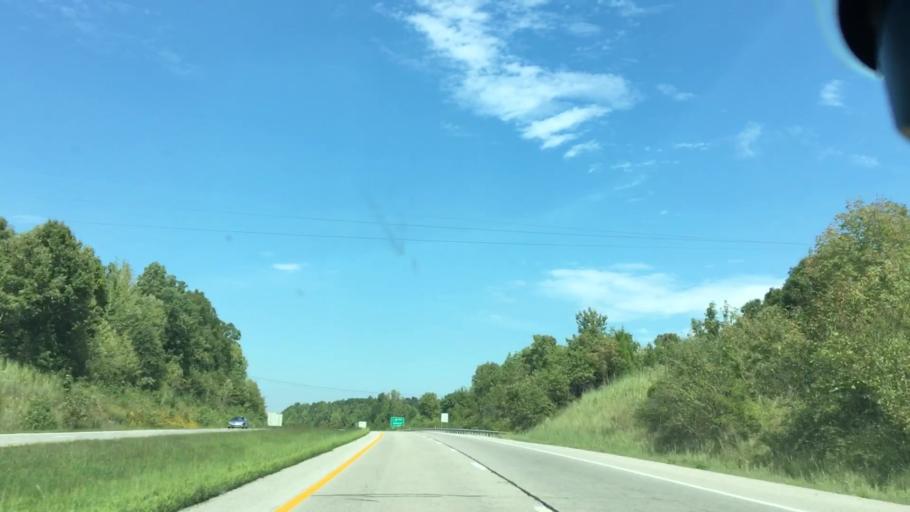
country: US
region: Kentucky
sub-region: Hopkins County
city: Nortonville
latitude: 37.1990
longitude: -87.4395
